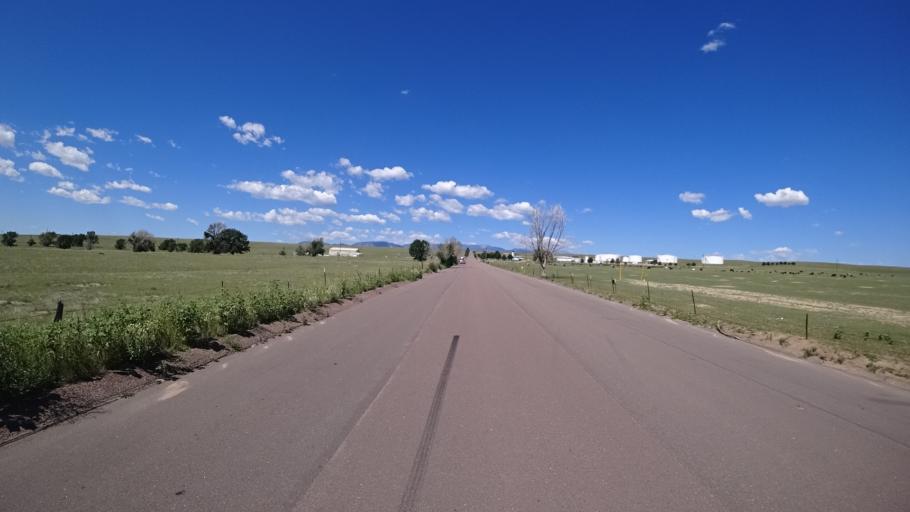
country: US
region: Colorado
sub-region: El Paso County
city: Security-Widefield
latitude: 38.7809
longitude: -104.6703
